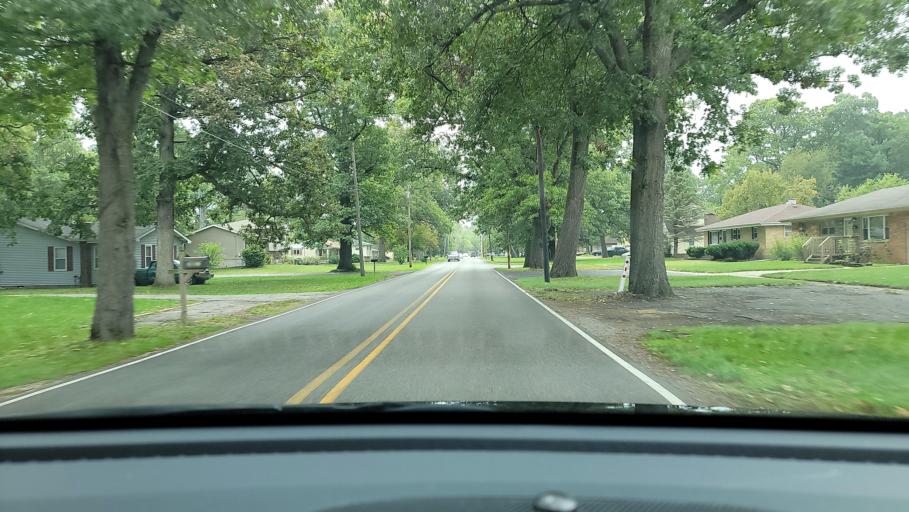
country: US
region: Indiana
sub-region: Lake County
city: Lake Station
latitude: 41.5676
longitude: -87.2219
